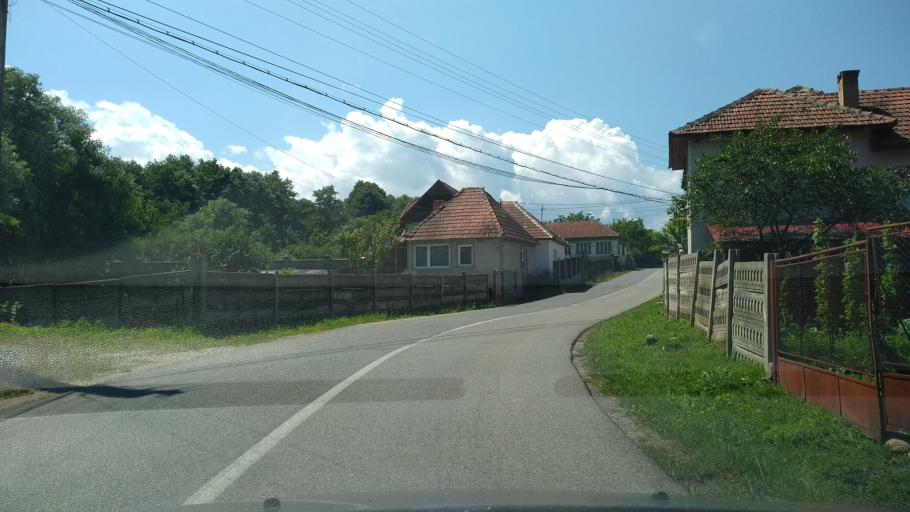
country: RO
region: Hunedoara
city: Bucium-Orlea
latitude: 45.5450
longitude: 22.9879
